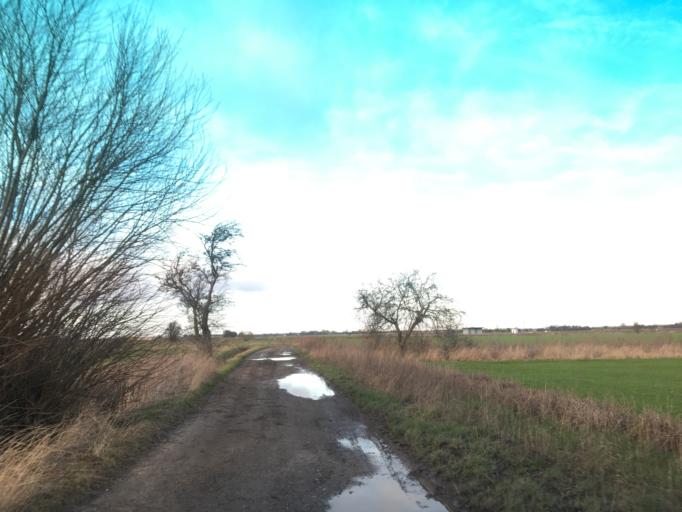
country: DK
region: Capital Region
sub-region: Tarnby Kommune
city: Tarnby
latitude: 55.5881
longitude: 12.6121
